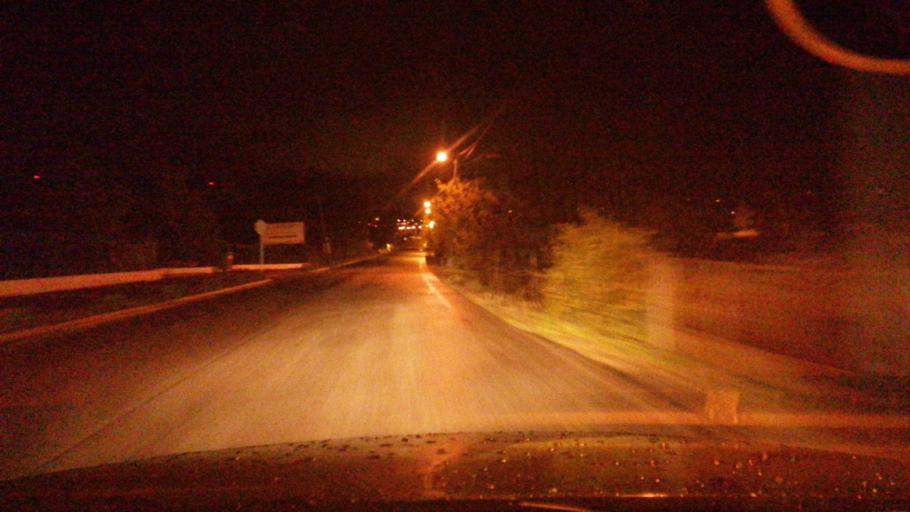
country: PT
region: Viseu
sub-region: Sernancelhe
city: Sernancelhe
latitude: 40.9326
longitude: -7.5581
